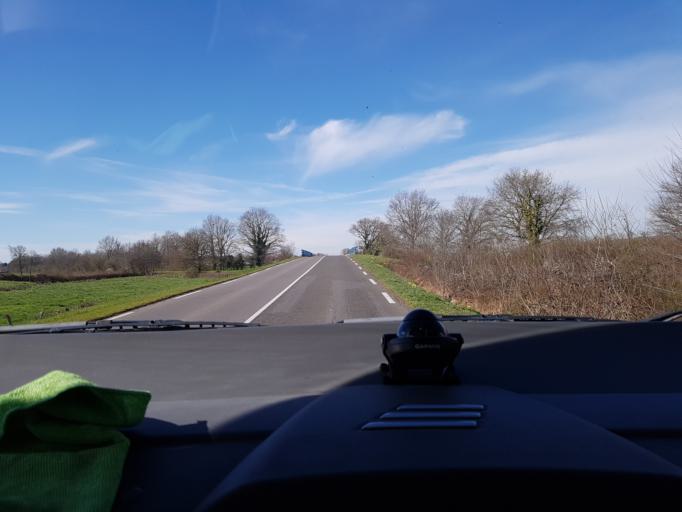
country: FR
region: Bourgogne
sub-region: Departement de Saone-et-Loire
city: Digoin
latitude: 46.5064
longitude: 4.0234
